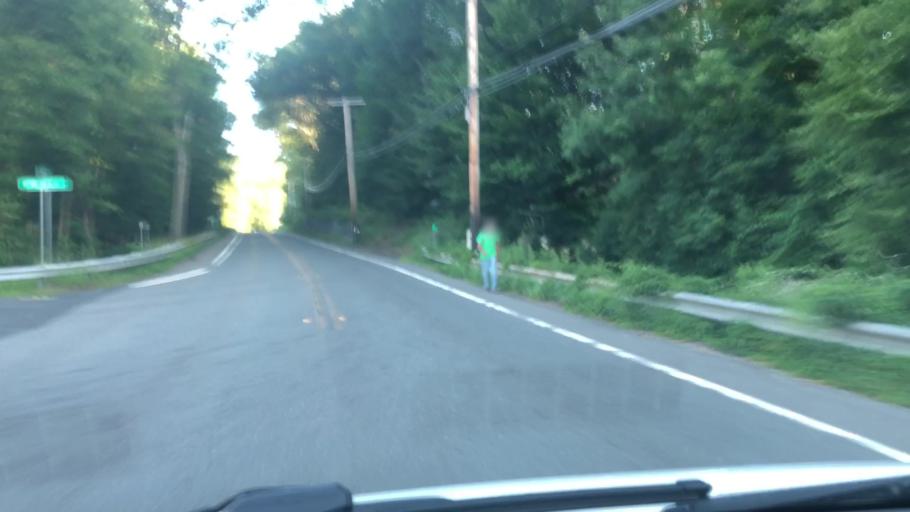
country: US
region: Massachusetts
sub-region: Hampshire County
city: Williamsburg
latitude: 42.4045
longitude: -72.7507
